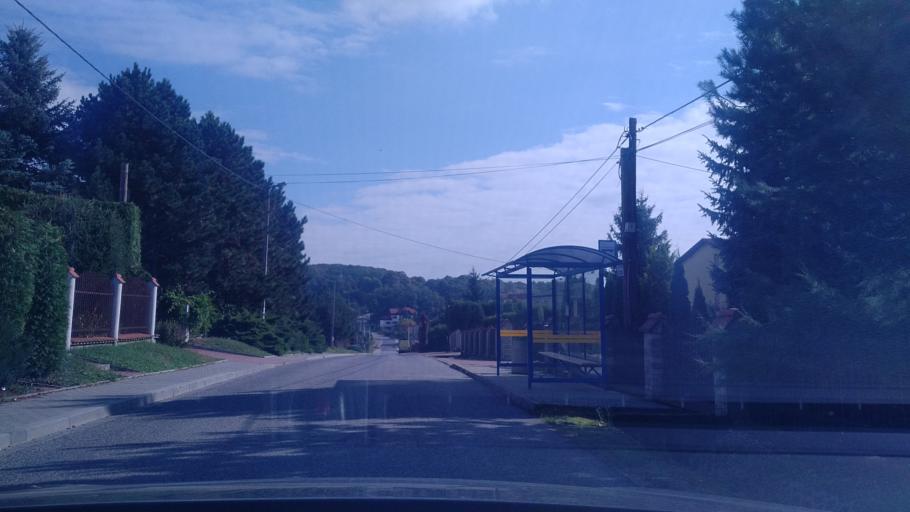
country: PL
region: Lesser Poland Voivodeship
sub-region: Powiat krakowski
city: Modlnica
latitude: 50.1336
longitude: 19.8555
